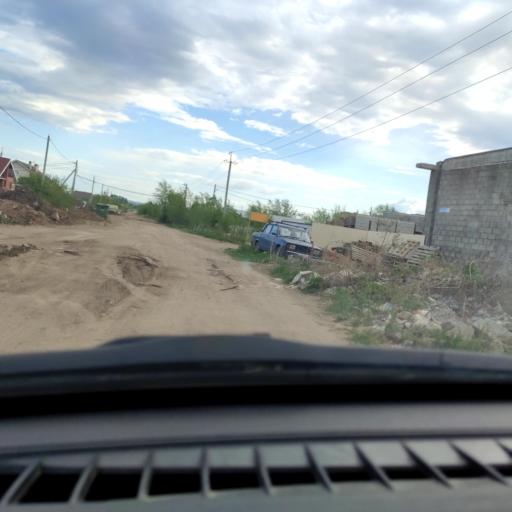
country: RU
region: Samara
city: Tol'yatti
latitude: 53.5757
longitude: 49.4143
